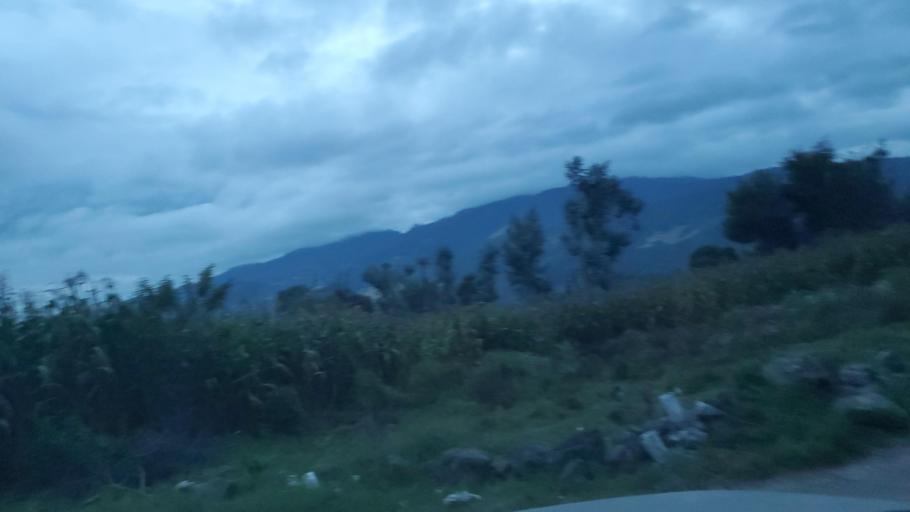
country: GT
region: Quetzaltenango
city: Quetzaltenango
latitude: 14.8262
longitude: -91.5395
